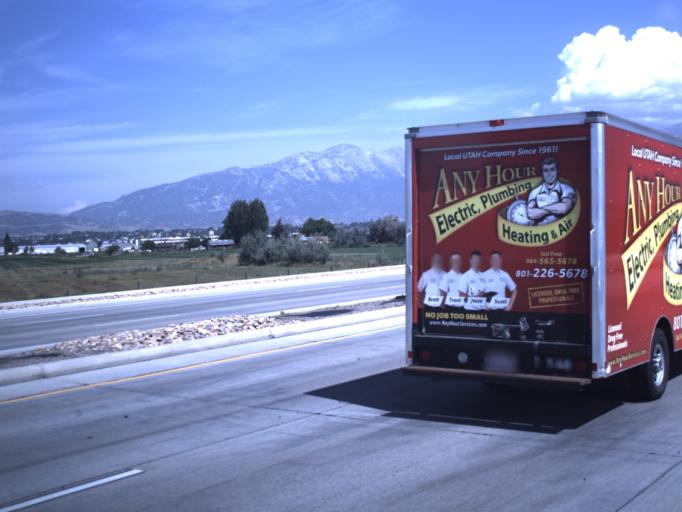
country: US
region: Utah
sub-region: Utah County
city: Lehi
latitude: 40.3742
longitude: -111.8388
